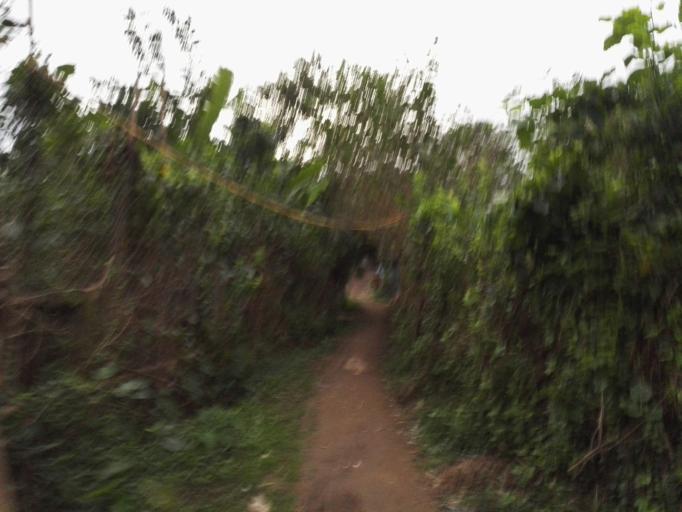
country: VN
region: Ha Noi
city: Hoan Kiem
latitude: 21.0428
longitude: 105.8533
